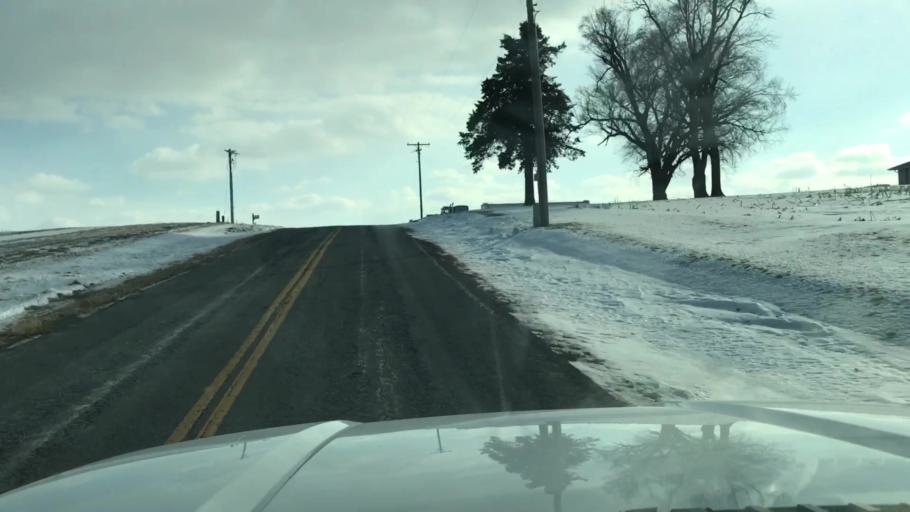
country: US
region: Missouri
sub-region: Nodaway County
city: Maryville
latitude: 40.1886
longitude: -95.0122
